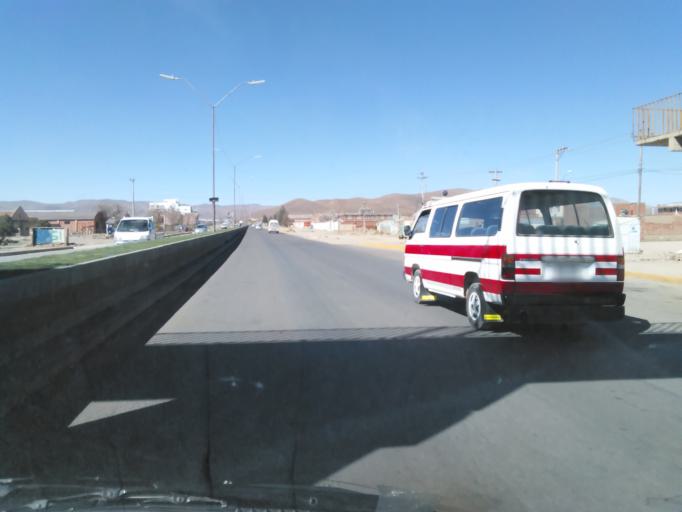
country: BO
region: Oruro
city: Oruro
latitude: -17.9763
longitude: -67.0684
